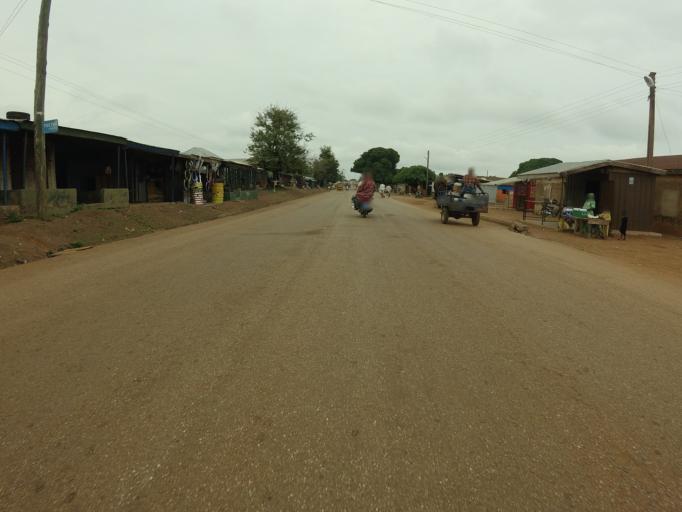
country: GH
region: Northern
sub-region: Yendi
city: Yendi
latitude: 9.4496
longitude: -0.0080
